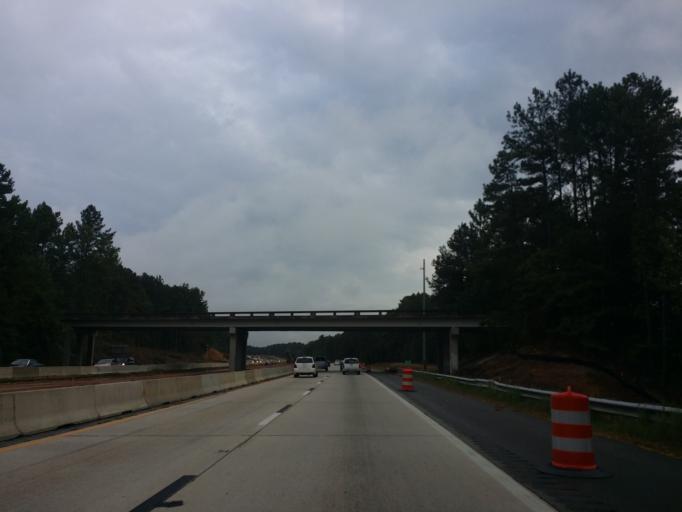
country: US
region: North Carolina
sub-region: Durham County
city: Durham
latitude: 35.9558
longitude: -78.8639
